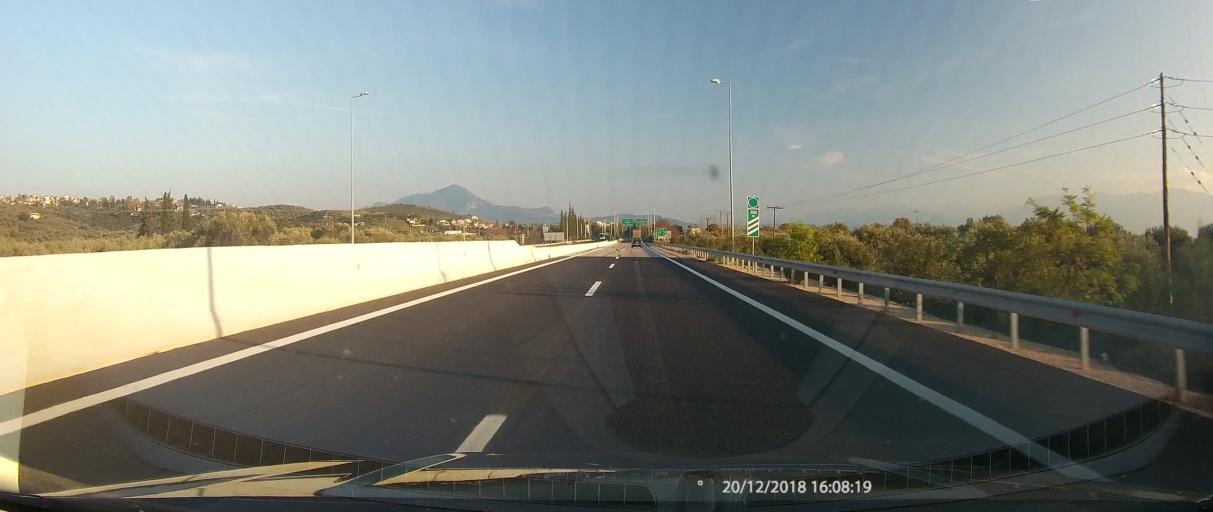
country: GR
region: Central Greece
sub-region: Nomos Fthiotidos
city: Pelasgia
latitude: 38.8869
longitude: 22.7624
